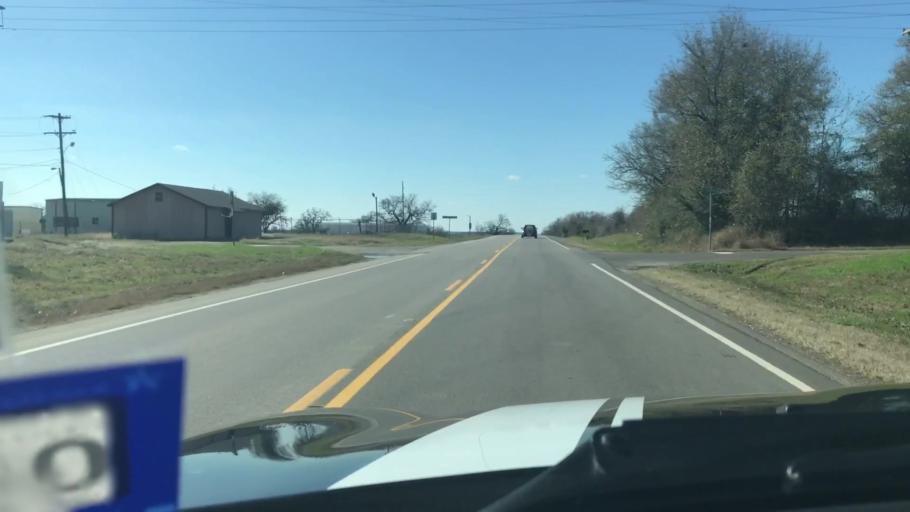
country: US
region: Texas
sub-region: Robertson County
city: Hearne
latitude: 30.8917
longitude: -96.6141
